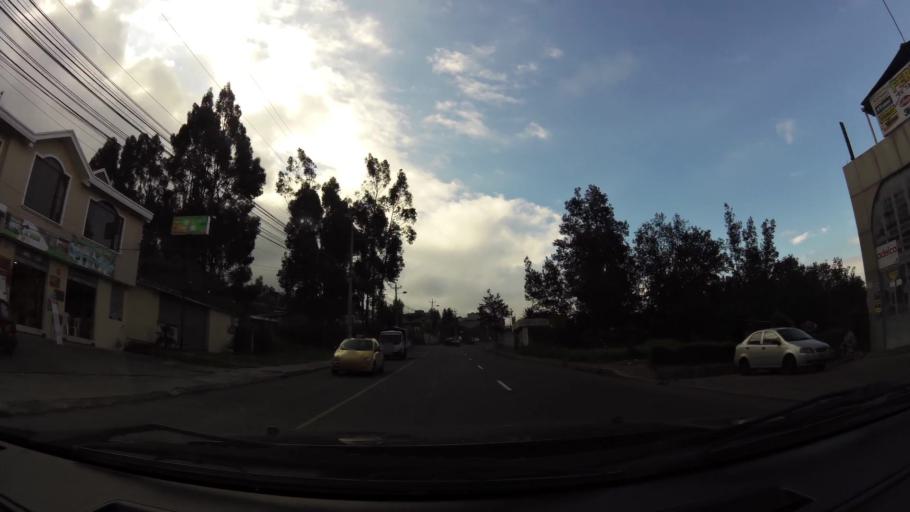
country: EC
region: Pichincha
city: Sangolqui
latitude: -0.2865
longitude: -78.4892
